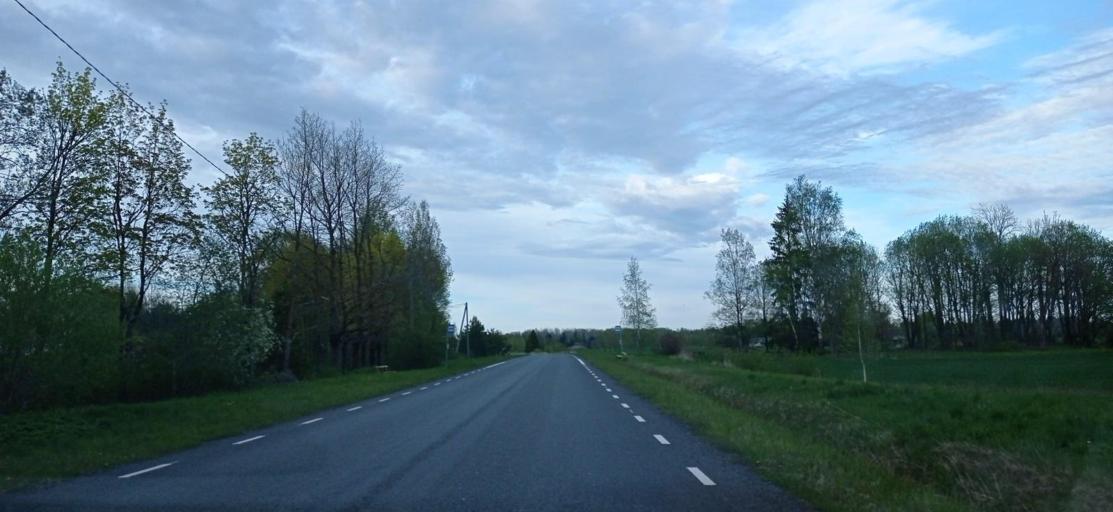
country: EE
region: Paernumaa
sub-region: Tootsi vald
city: Tootsi
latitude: 58.5435
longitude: 24.7642
